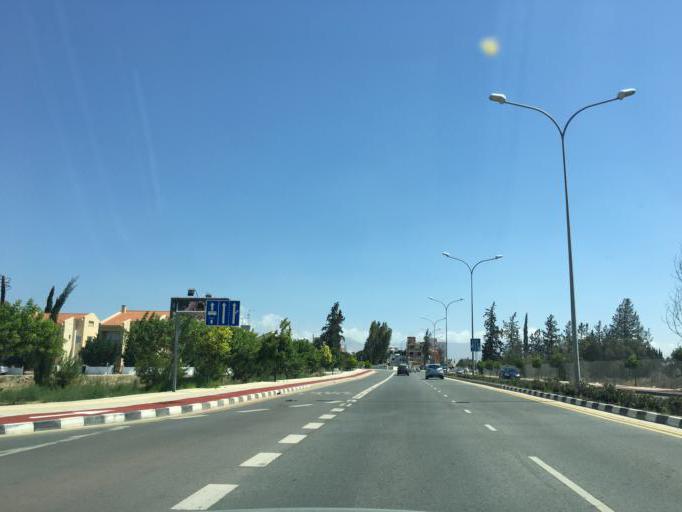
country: CY
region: Lefkosia
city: Nicosia
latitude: 35.1504
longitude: 33.3272
